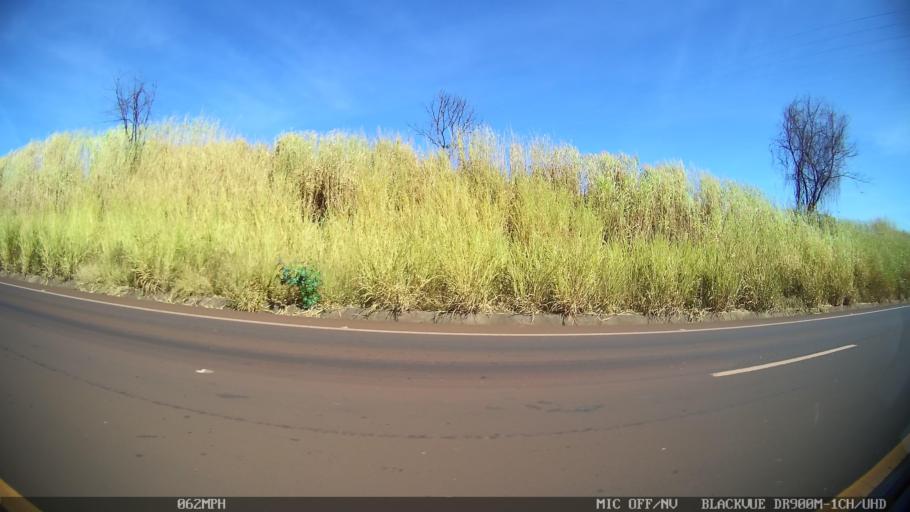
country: BR
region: Sao Paulo
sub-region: Nuporanga
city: Nuporanga
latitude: -20.5554
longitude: -47.6408
